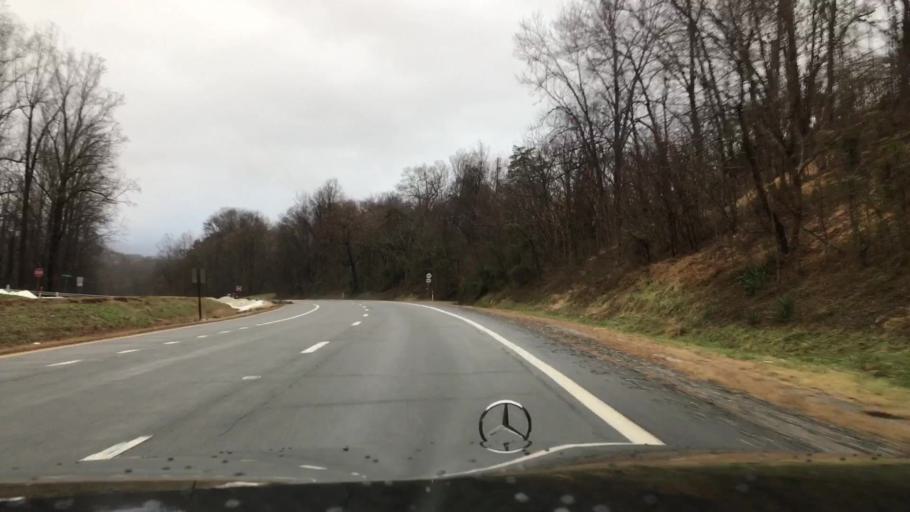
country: US
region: Virginia
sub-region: Nelson County
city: Nellysford
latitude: 37.8460
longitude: -78.8069
